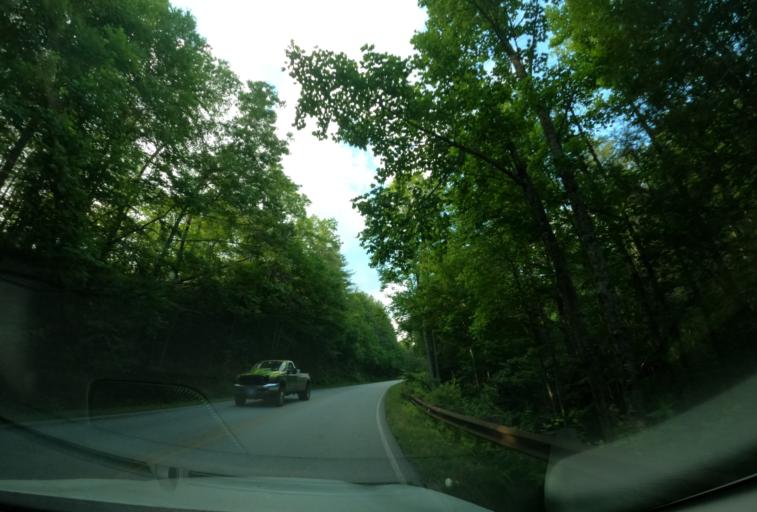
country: US
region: North Carolina
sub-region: Transylvania County
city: Brevard
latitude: 35.2169
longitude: -82.8571
